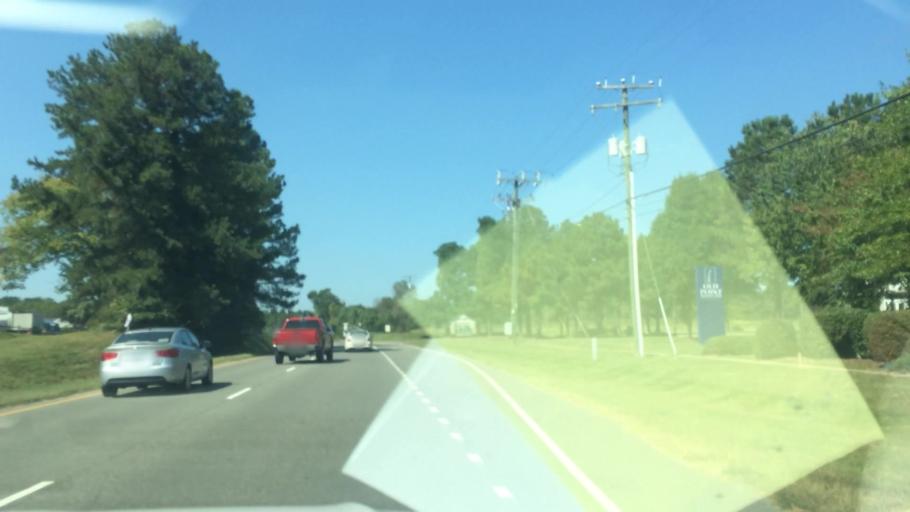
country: US
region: Virginia
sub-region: James City County
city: Williamsburg
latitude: 37.3712
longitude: -76.7742
